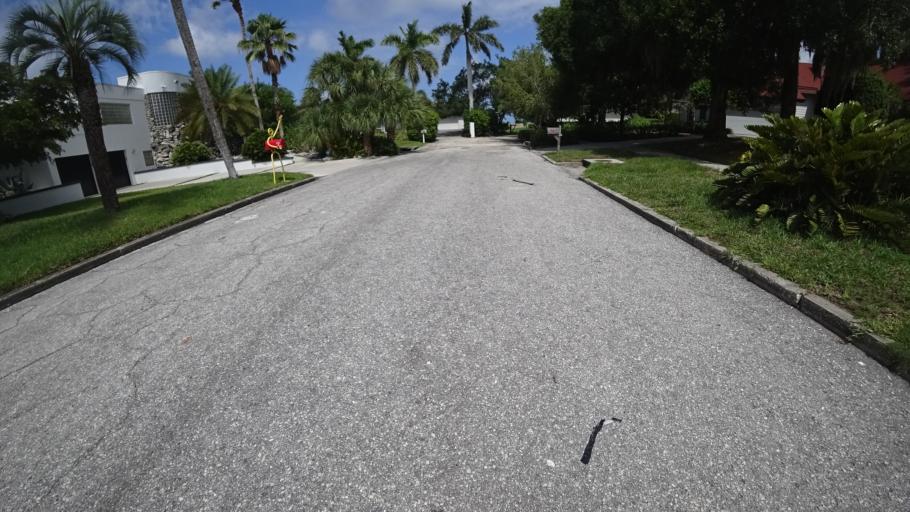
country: US
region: Florida
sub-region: Manatee County
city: Whitfield
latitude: 27.4025
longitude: -82.5706
